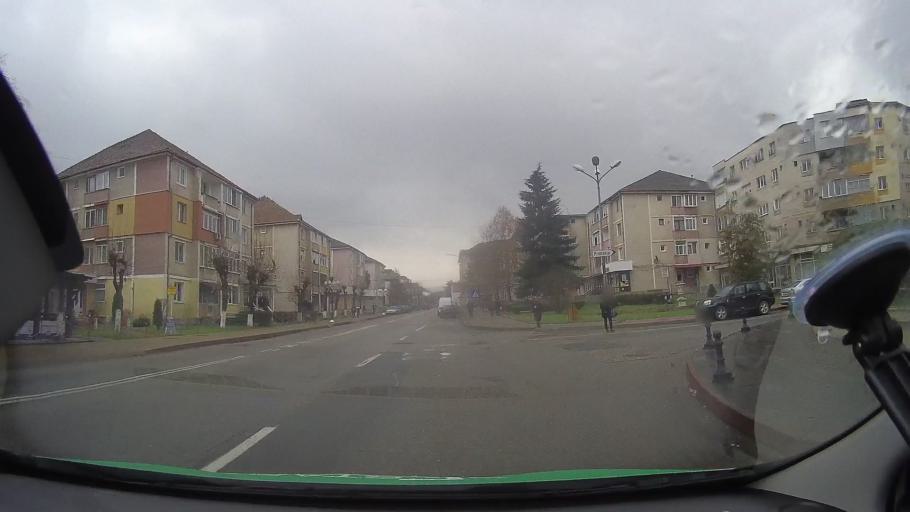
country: RO
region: Hunedoara
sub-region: Municipiul Brad
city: Brad
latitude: 46.1277
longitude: 22.7922
